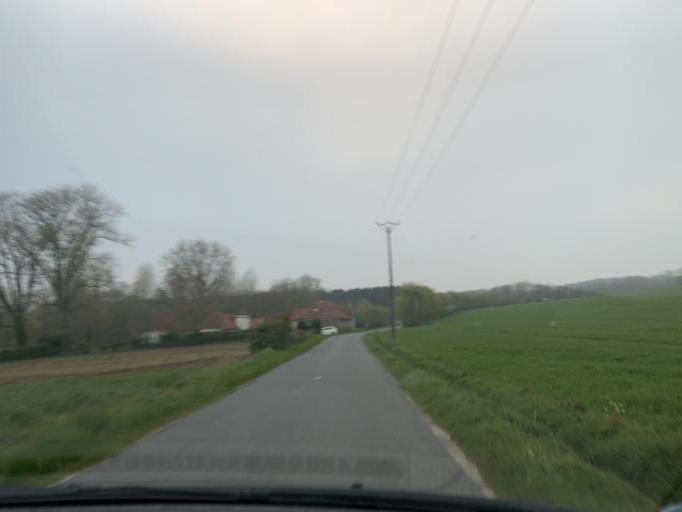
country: FR
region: Nord-Pas-de-Calais
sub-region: Departement du Pas-de-Calais
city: Wimille
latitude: 50.7628
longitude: 1.6411
